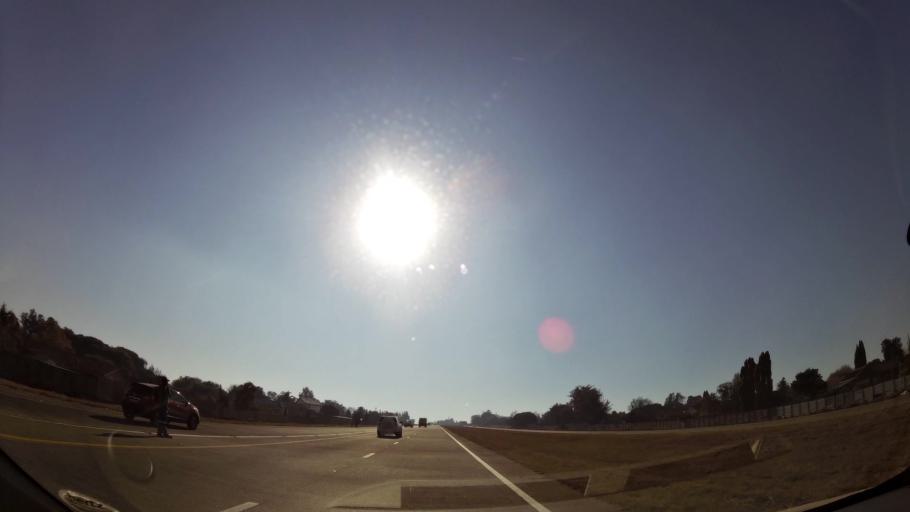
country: ZA
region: Mpumalanga
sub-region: Nkangala District Municipality
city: Witbank
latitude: -25.9137
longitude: 29.2383
